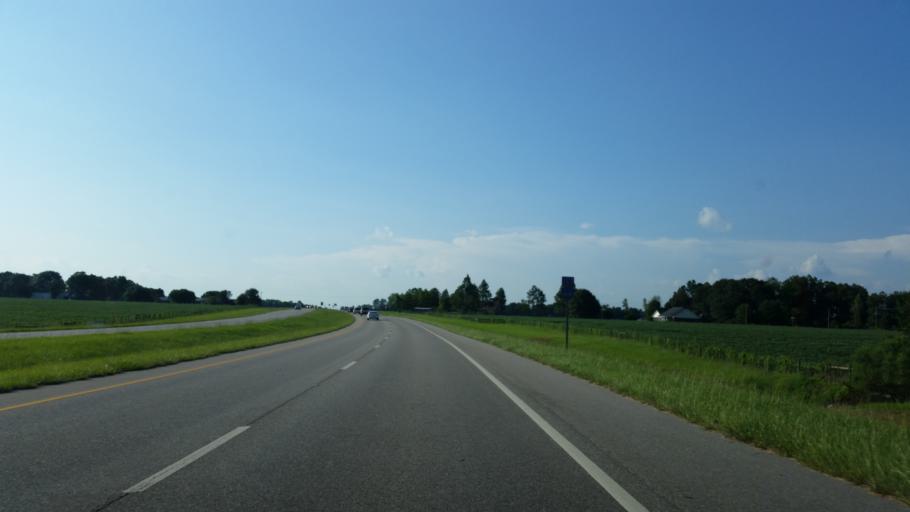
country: US
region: Alabama
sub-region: Baldwin County
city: Robertsdale
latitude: 30.6149
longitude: -87.6667
